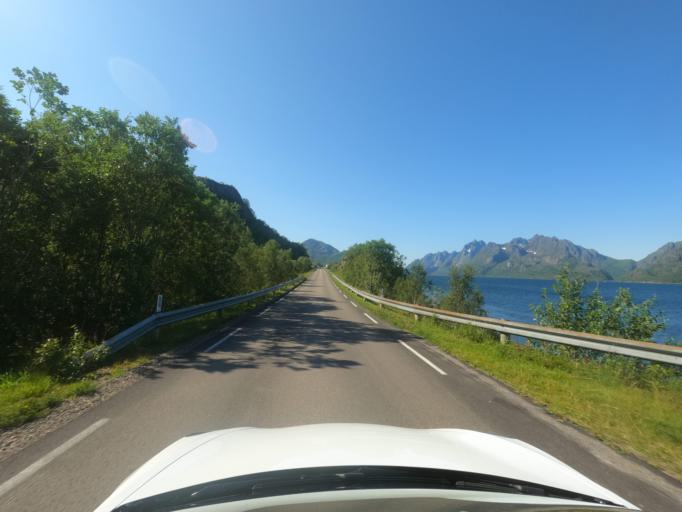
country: NO
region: Nordland
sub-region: Hadsel
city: Stokmarknes
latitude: 68.3278
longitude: 15.0135
